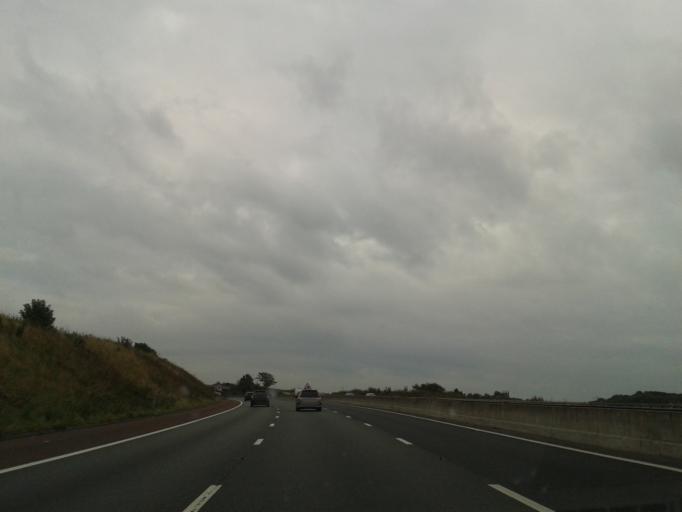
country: GB
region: England
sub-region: Lancashire
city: Bolton le Sands
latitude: 54.0624
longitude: -2.7712
